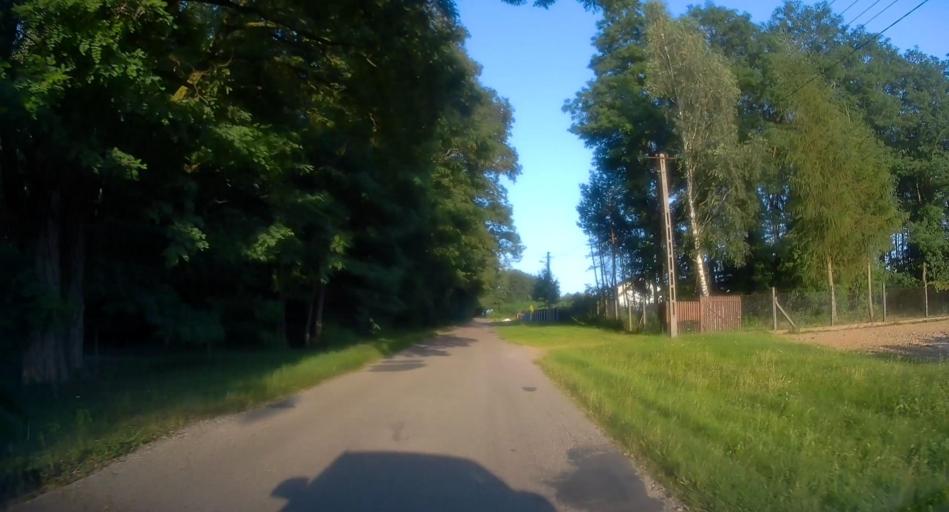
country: PL
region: Lodz Voivodeship
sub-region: Powiat skierniewicki
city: Kowiesy
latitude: 51.9023
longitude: 20.3636
